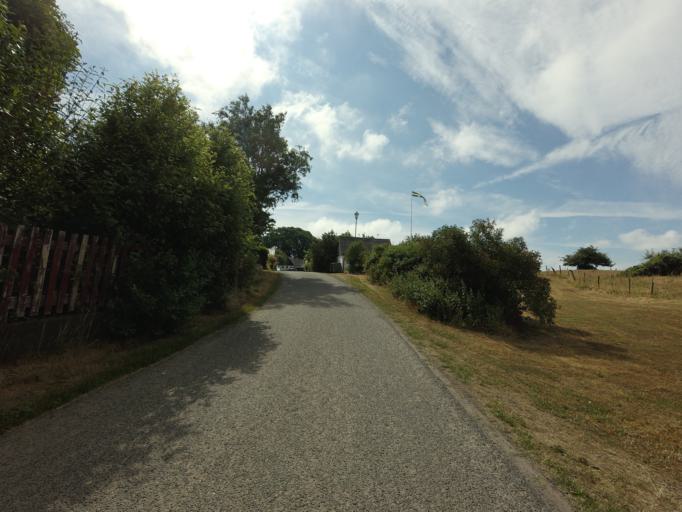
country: SE
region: Skane
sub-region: Simrishamns Kommun
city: Simrishamn
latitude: 55.4874
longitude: 14.3147
